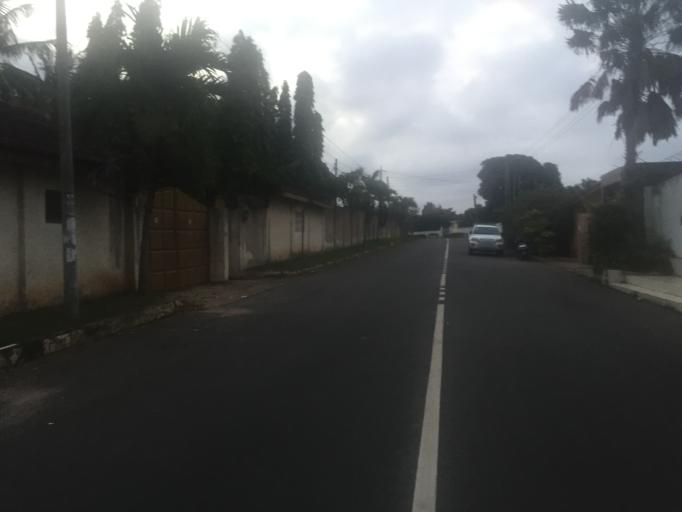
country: GH
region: Greater Accra
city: Dome
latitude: 5.6050
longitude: -0.2275
